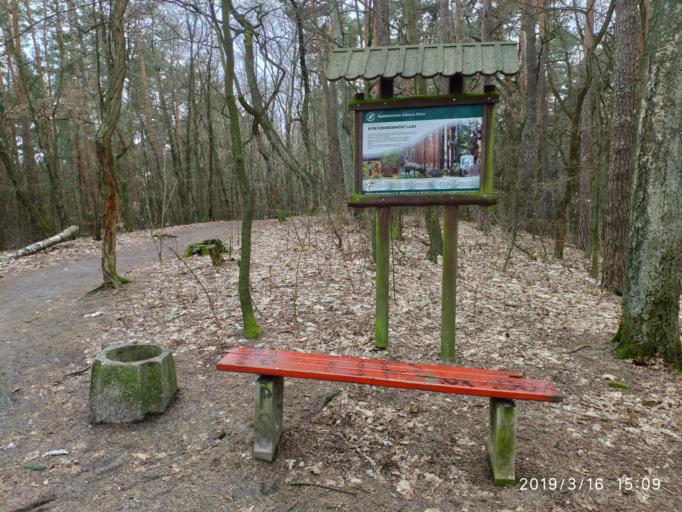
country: PL
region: Lubusz
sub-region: Zielona Gora
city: Zielona Gora
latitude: 51.9239
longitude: 15.4819
